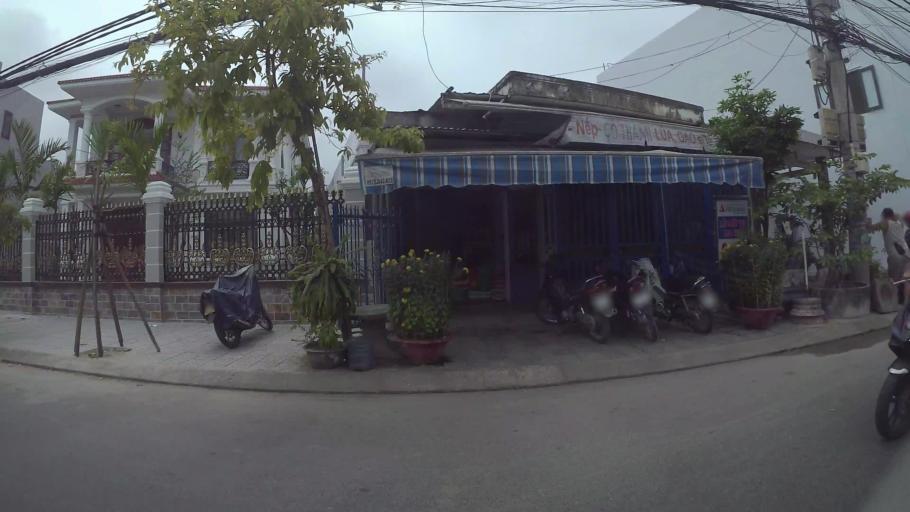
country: VN
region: Da Nang
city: Lien Chieu
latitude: 16.0647
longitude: 108.1668
